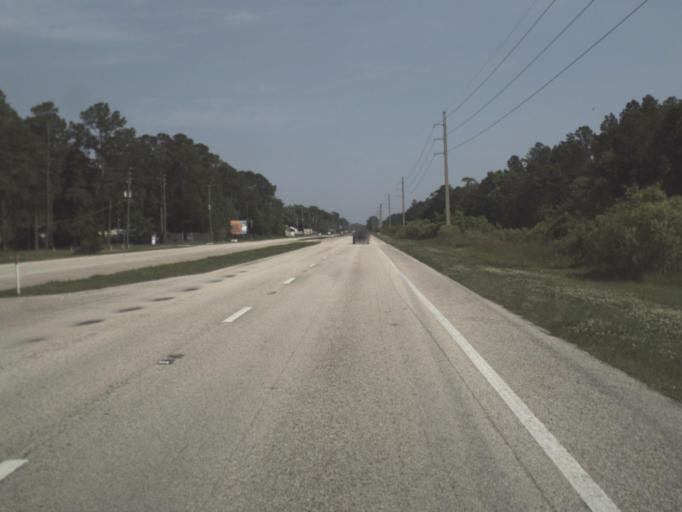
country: US
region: Florida
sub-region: Saint Johns County
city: Villano Beach
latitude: 29.9859
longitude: -81.3683
